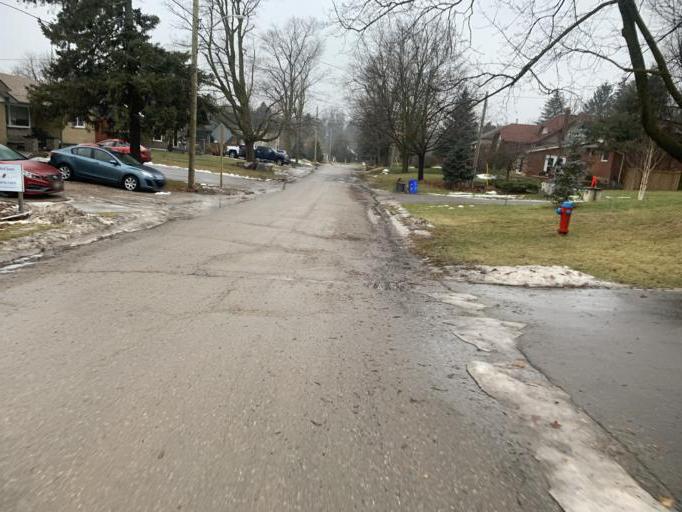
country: CA
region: Ontario
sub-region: Halton
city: Milton
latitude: 43.6605
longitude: -79.9324
